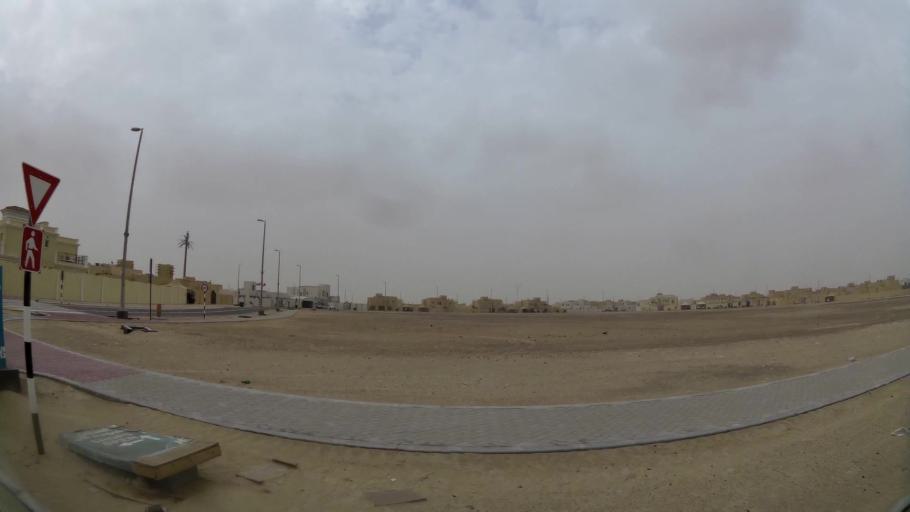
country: AE
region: Abu Dhabi
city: Abu Dhabi
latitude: 24.4542
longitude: 54.7359
